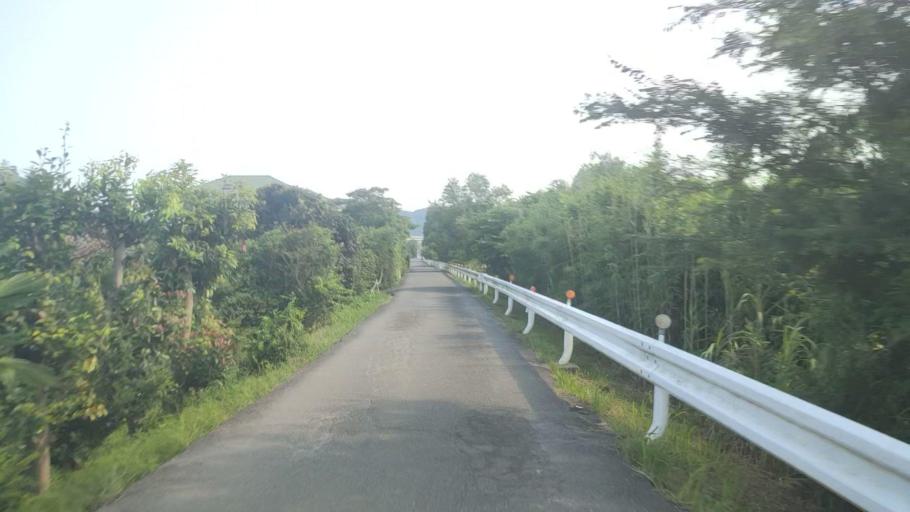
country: JP
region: Kanagawa
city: Hiratsuka
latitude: 35.3426
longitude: 139.3233
